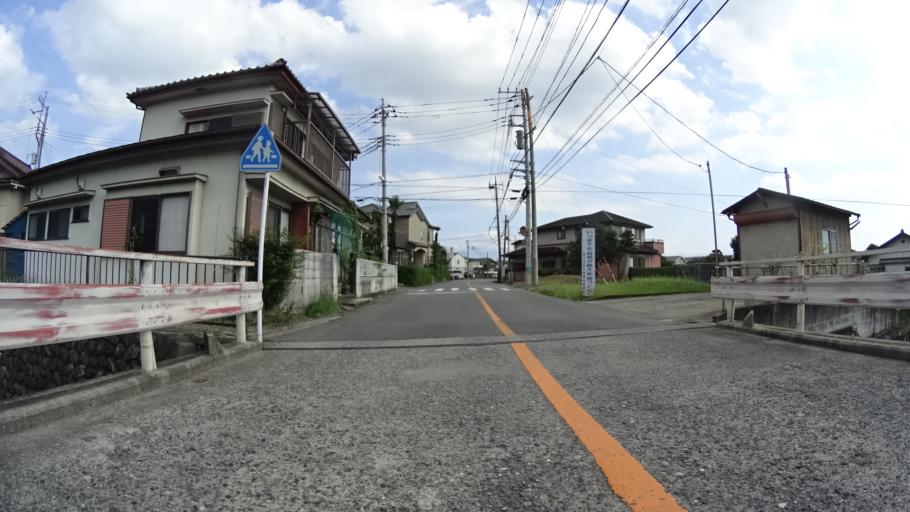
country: JP
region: Yamanashi
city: Kofu-shi
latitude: 35.6854
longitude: 138.5657
